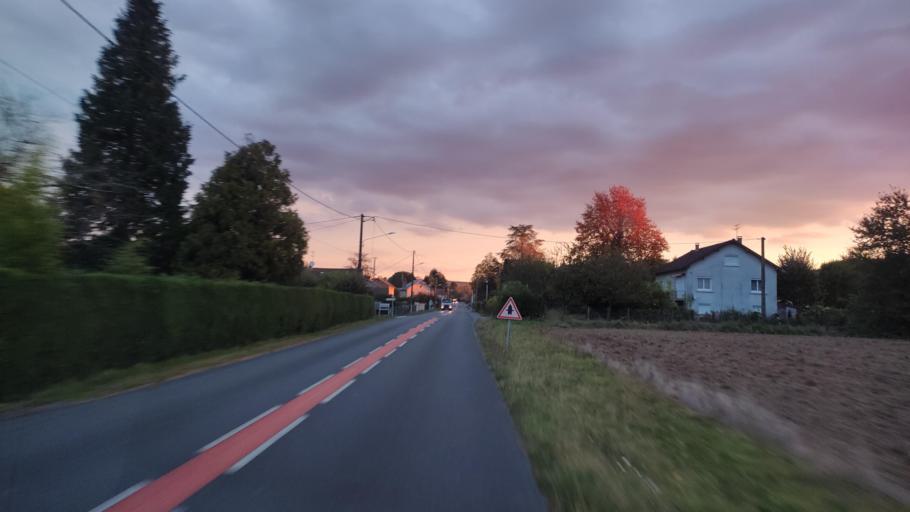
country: FR
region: Limousin
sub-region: Departement de la Haute-Vienne
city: Rilhac-Rancon
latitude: 45.9212
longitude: 1.3403
